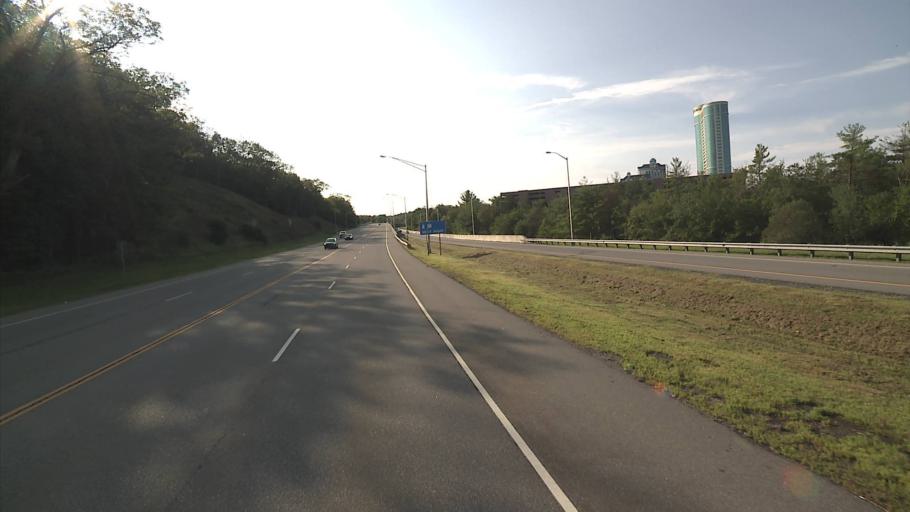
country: US
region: Connecticut
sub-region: New London County
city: Preston City
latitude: 41.4809
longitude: -71.9656
